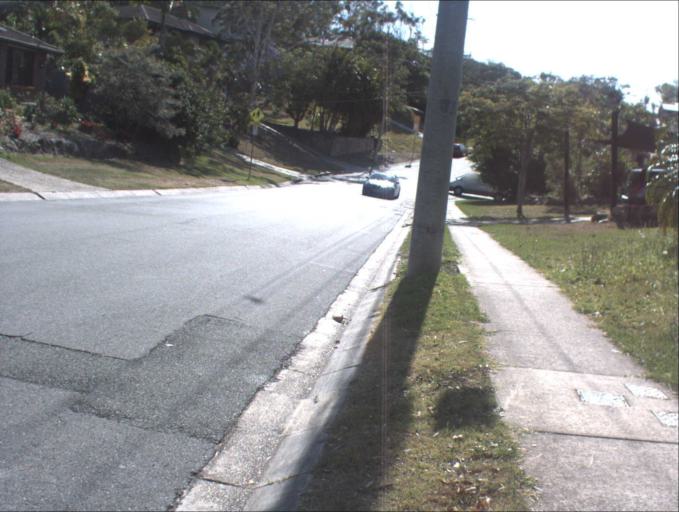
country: AU
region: Queensland
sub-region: Logan
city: Slacks Creek
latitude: -27.6494
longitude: 153.1786
